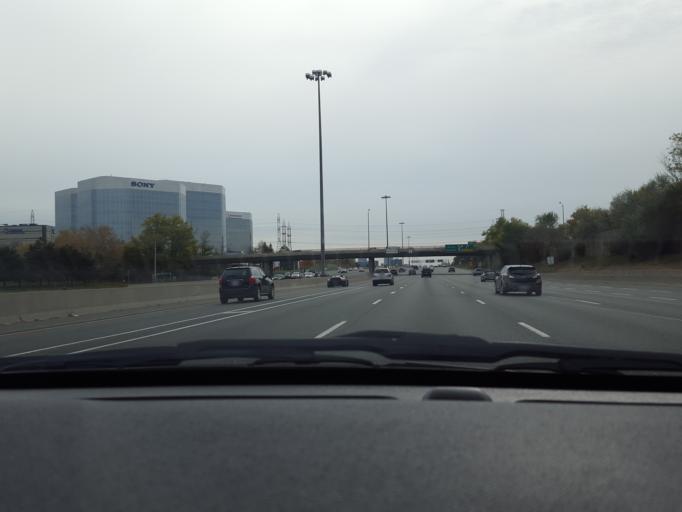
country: CA
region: Ontario
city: Willowdale
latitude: 43.8046
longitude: -79.3459
